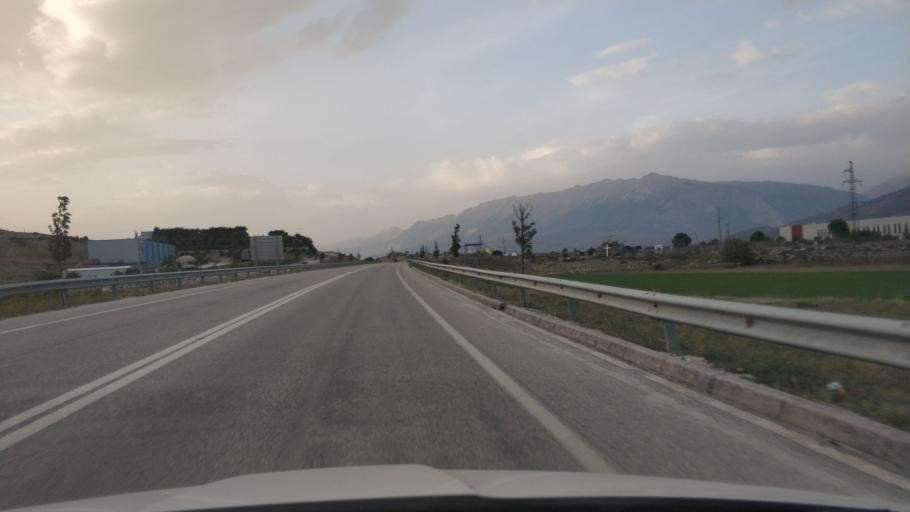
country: AL
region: Gjirokaster
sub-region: Rrethi i Gjirokastres
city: Libohove
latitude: 39.9712
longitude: 20.2365
